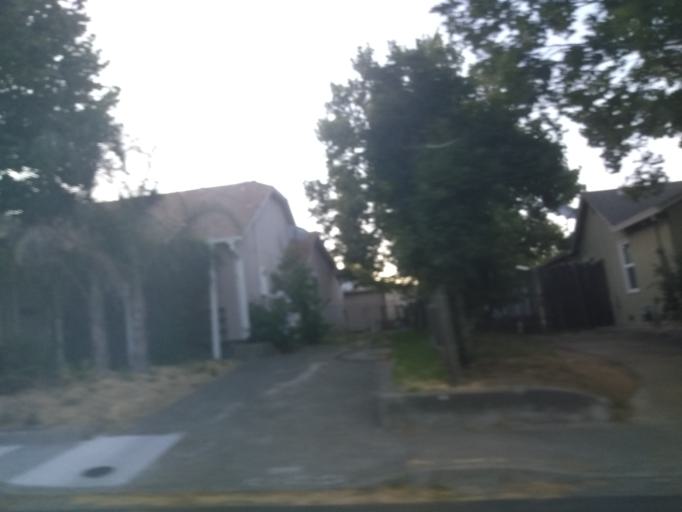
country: US
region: California
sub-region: Mendocino County
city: Ukiah
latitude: 39.1383
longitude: -123.2137
